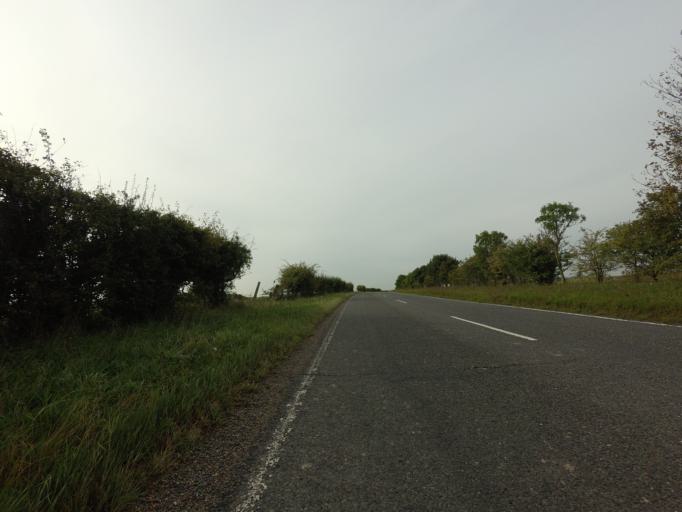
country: GB
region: England
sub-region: Cambridgeshire
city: Melbourn
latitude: 52.0799
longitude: 0.0688
